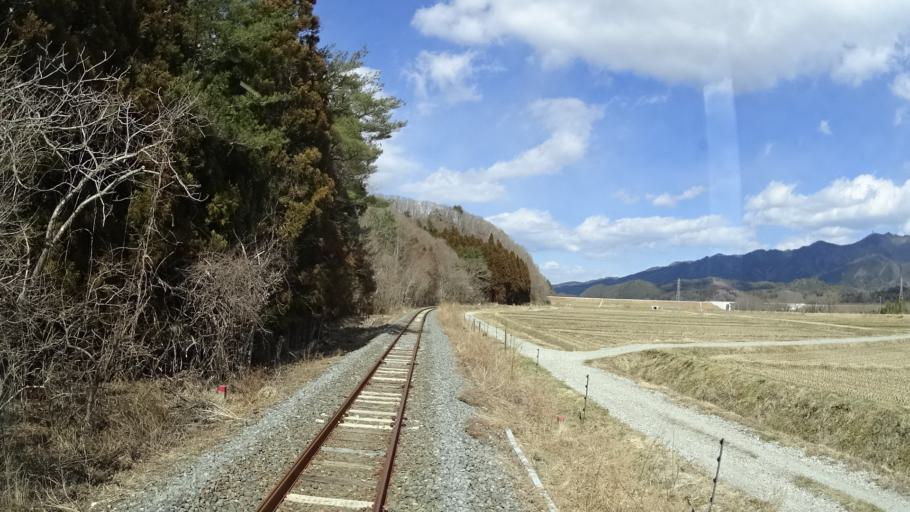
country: JP
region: Iwate
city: Yamada
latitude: 39.5214
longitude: 141.9173
